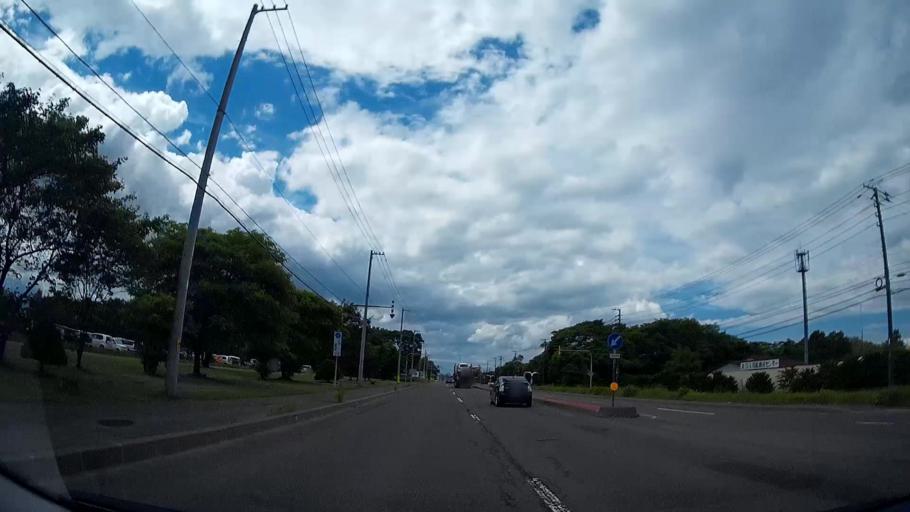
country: JP
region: Hokkaido
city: Chitose
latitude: 42.8667
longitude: 141.5929
